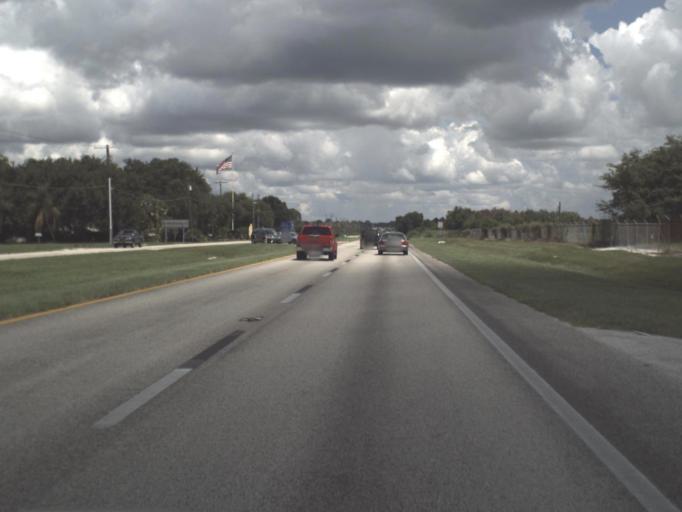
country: US
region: Florida
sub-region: Polk County
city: Inwood
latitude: 28.0683
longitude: -81.7497
